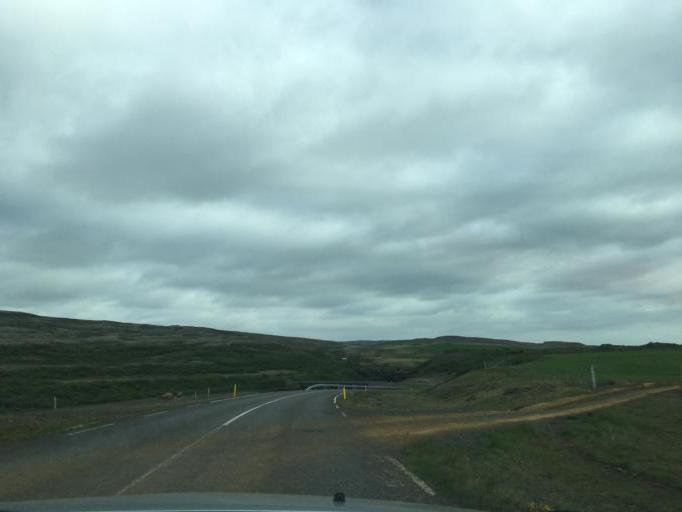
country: IS
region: South
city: Vestmannaeyjar
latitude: 64.2655
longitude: -20.2233
